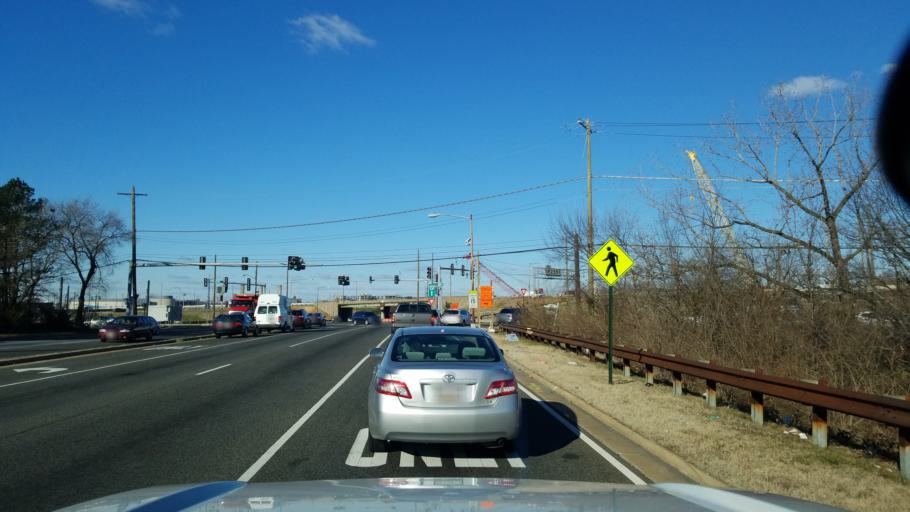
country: US
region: Maryland
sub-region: Prince George's County
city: Glassmanor
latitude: 38.8621
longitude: -76.9967
